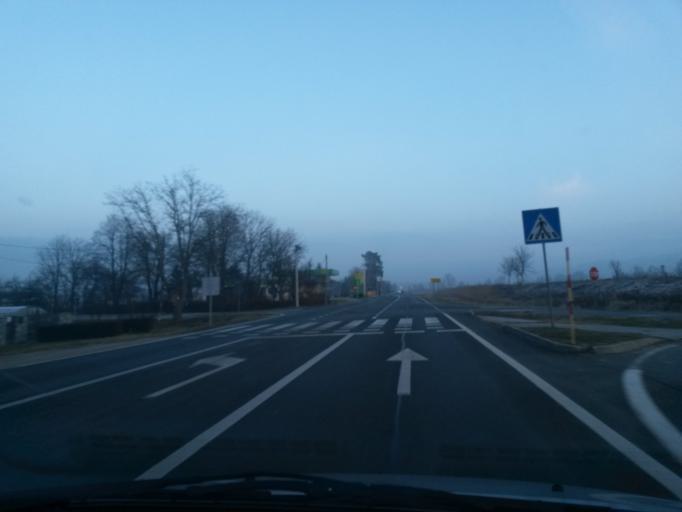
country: HR
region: Koprivnicko-Krizevacka
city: Reka
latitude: 46.1992
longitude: 16.7168
